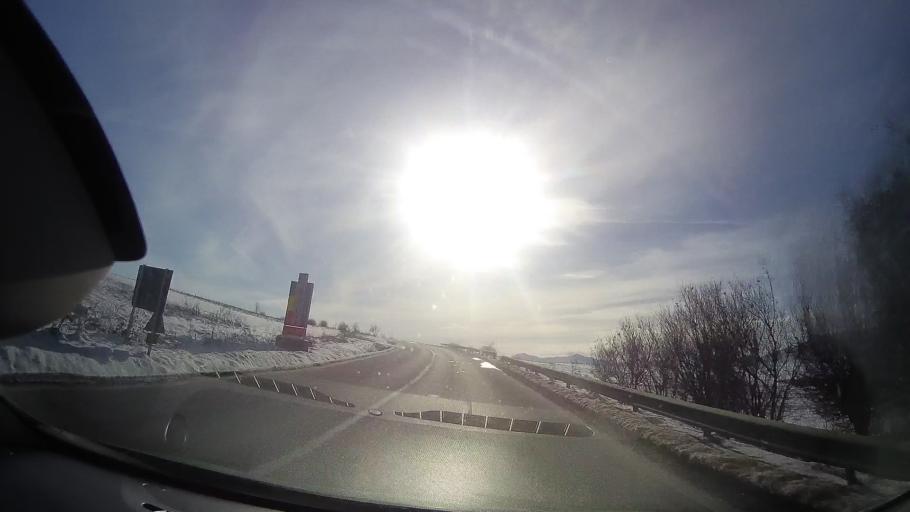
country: RO
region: Neamt
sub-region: Comuna Baltatesti
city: Valea Seaca
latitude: 47.1642
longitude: 26.3182
